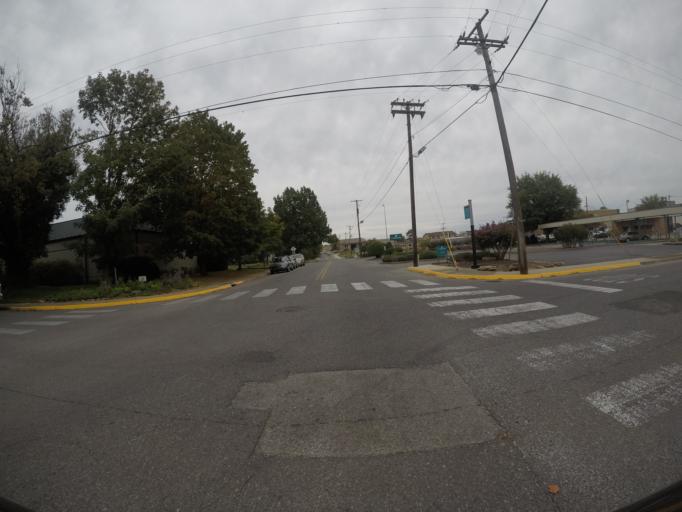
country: US
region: Arkansas
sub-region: Washington County
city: Springdale
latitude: 36.1864
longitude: -94.1323
